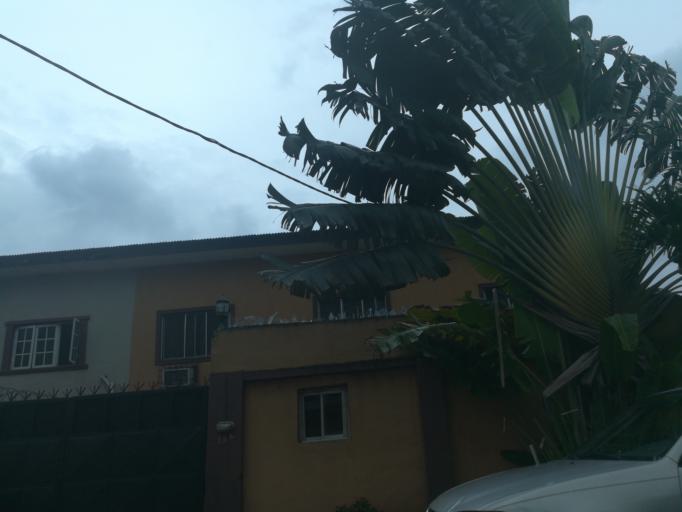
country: NG
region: Lagos
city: Ikeja
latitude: 6.6142
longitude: 3.3474
